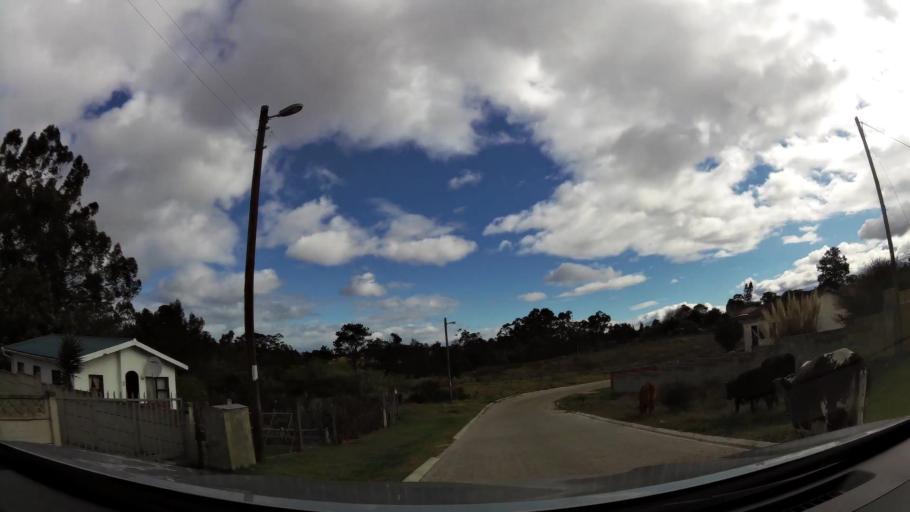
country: ZA
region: Western Cape
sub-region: Eden District Municipality
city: George
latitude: -34.0269
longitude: 22.4666
